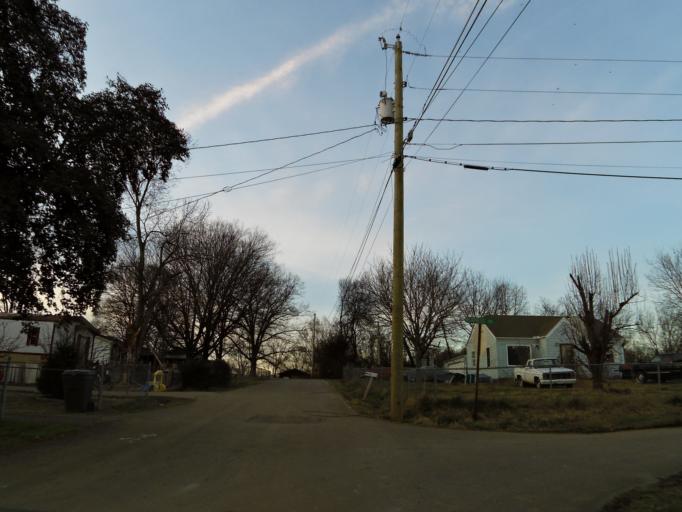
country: US
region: Tennessee
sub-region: Blount County
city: Eagleton Village
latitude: 35.8258
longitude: -83.9484
